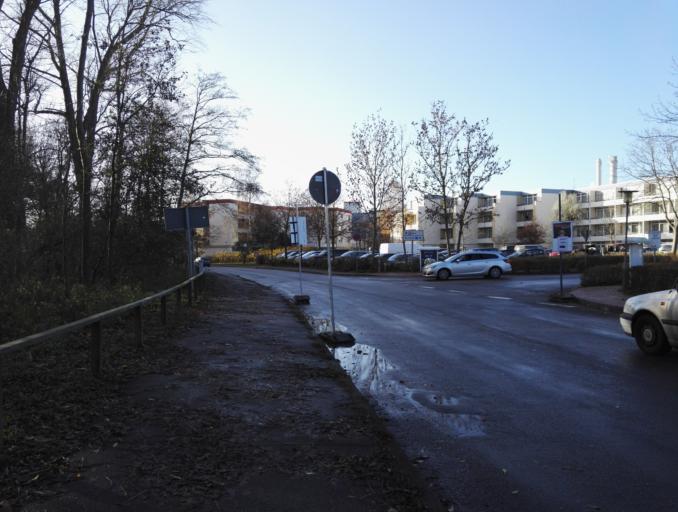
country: DE
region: Schleswig-Holstein
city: Wangels
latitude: 54.3100
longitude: 10.8004
